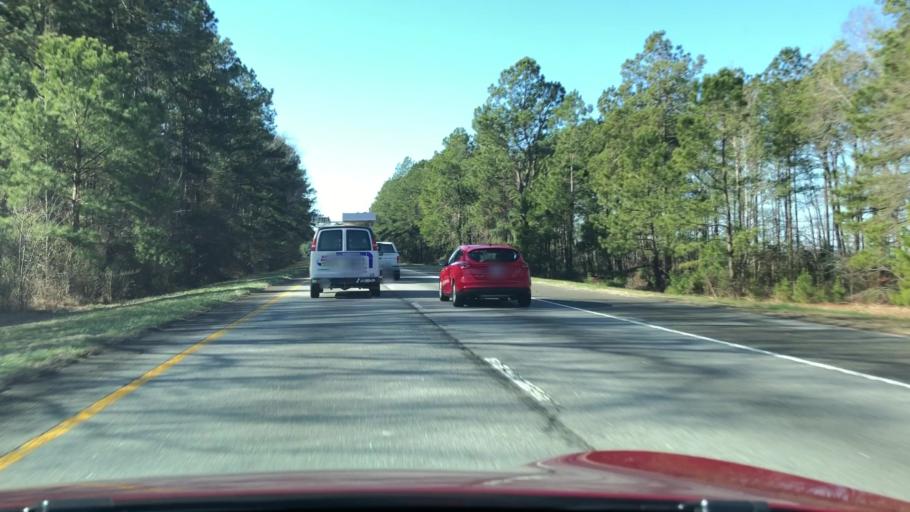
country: US
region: South Carolina
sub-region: Clarendon County
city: Manning
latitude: 33.5668
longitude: -80.3899
